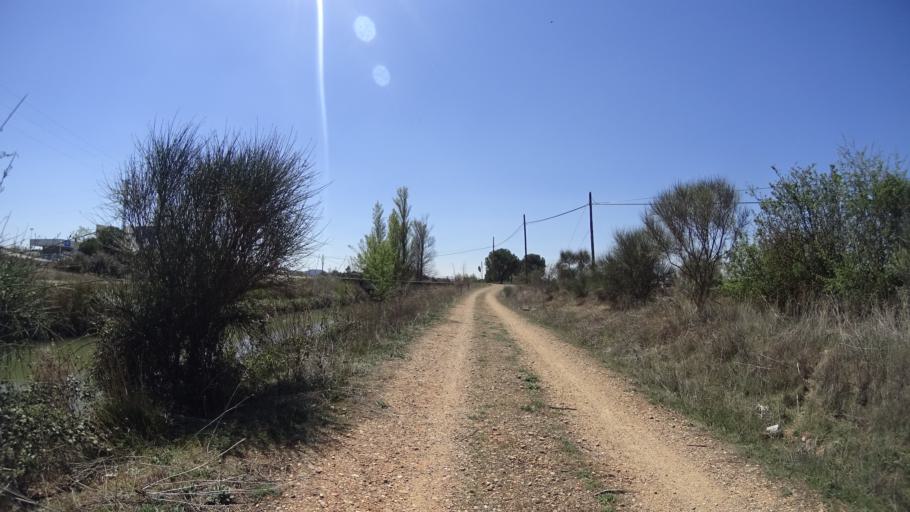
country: ES
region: Castille and Leon
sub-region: Provincia de Palencia
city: Duenas
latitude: 41.8372
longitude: -4.5649
